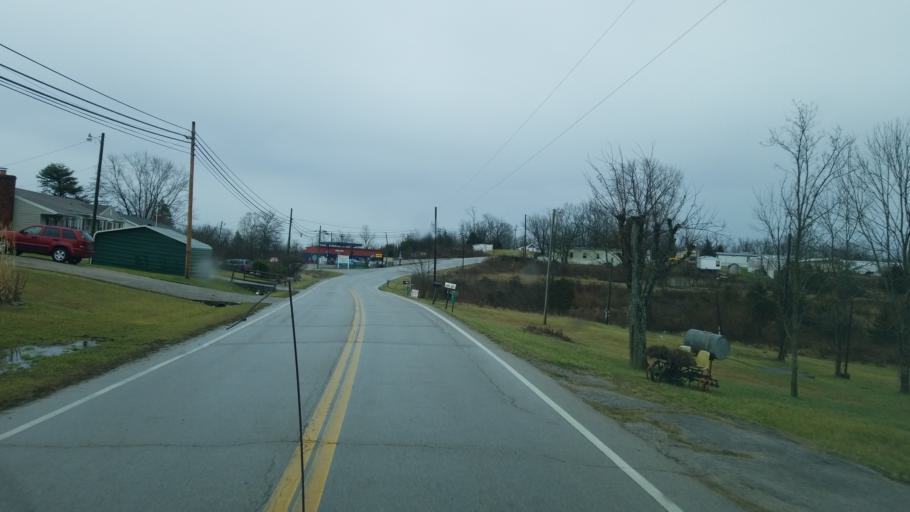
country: US
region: Kentucky
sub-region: Mason County
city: Maysville
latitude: 38.6001
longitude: -83.6739
